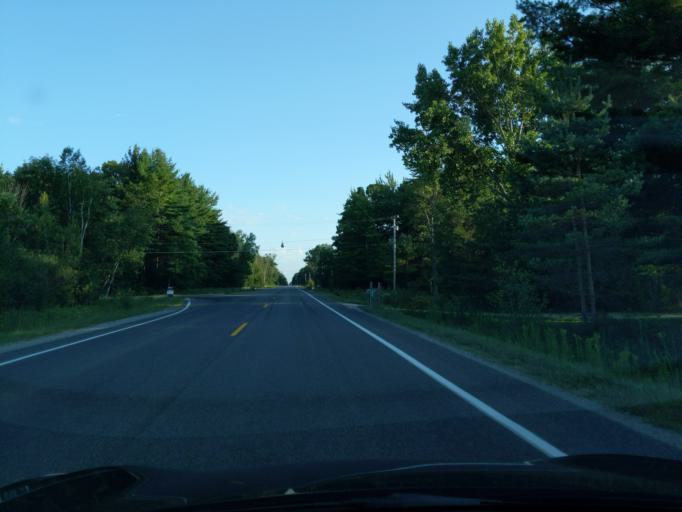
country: US
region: Michigan
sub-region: Midland County
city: Midland
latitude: 43.5404
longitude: -84.3698
